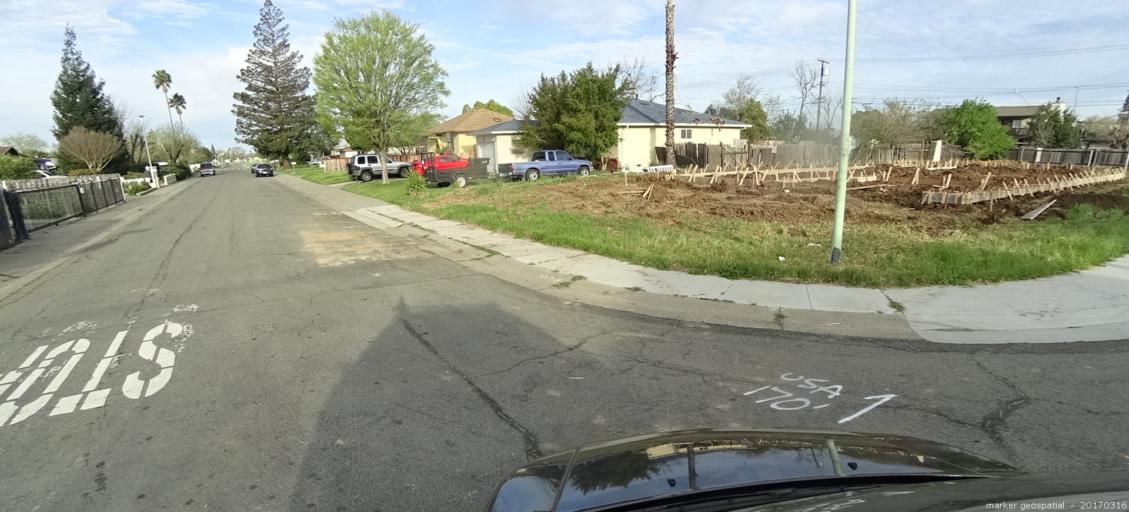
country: US
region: California
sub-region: Sacramento County
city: Parkway
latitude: 38.5092
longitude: -121.4788
